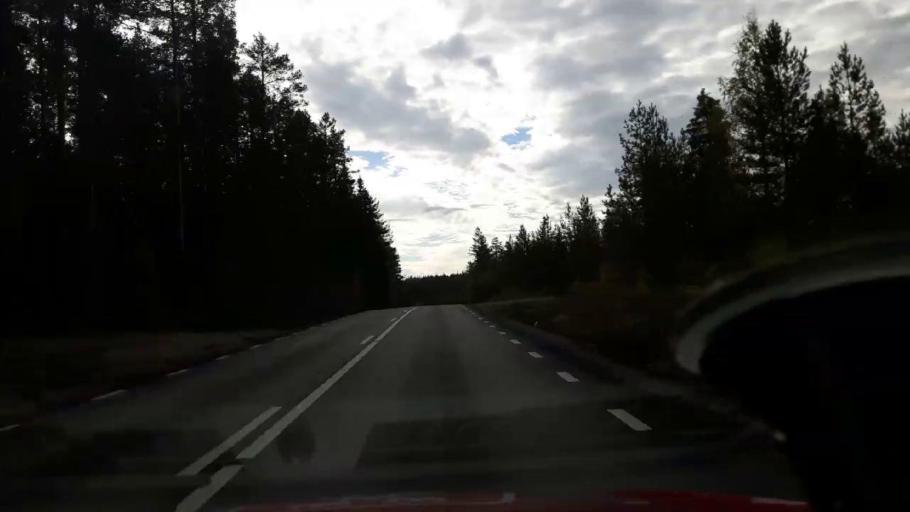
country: SE
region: Gaevleborg
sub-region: Ljusdals Kommun
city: Farila
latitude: 61.9500
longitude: 15.3687
